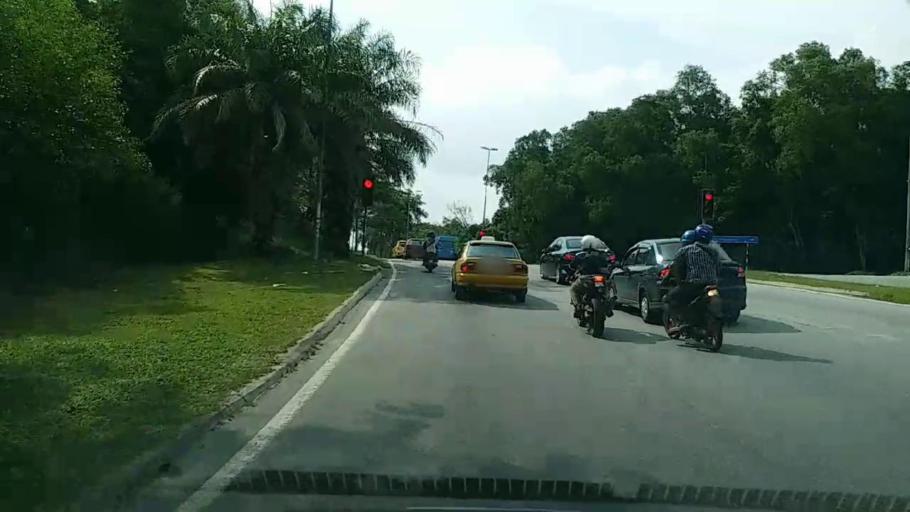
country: MY
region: Putrajaya
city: Putrajaya
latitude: 2.9627
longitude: 101.6174
